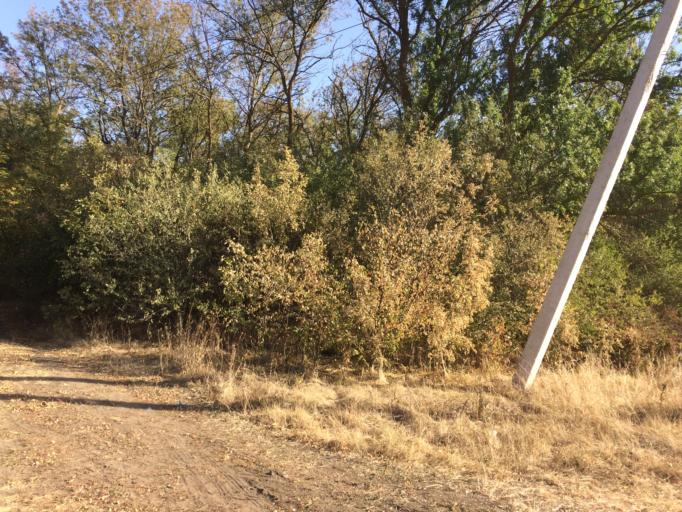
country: RU
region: Rostov
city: Tselina
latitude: 46.5219
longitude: 41.1802
